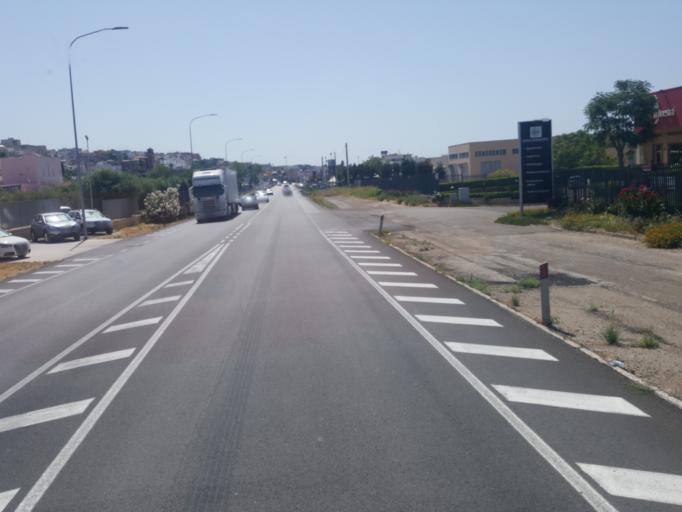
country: IT
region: Apulia
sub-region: Provincia di Taranto
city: Massafra
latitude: 40.5884
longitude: 17.1027
